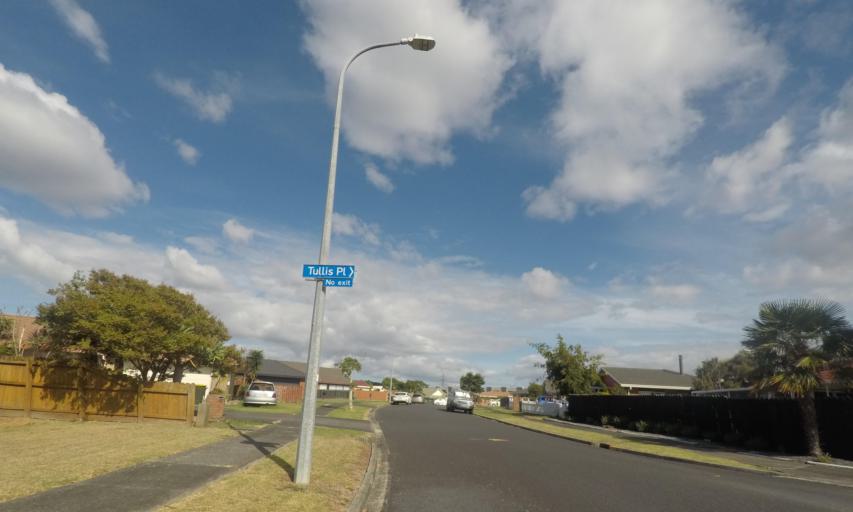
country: NZ
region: Auckland
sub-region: Auckland
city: Pakuranga
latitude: -36.9238
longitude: 174.8970
